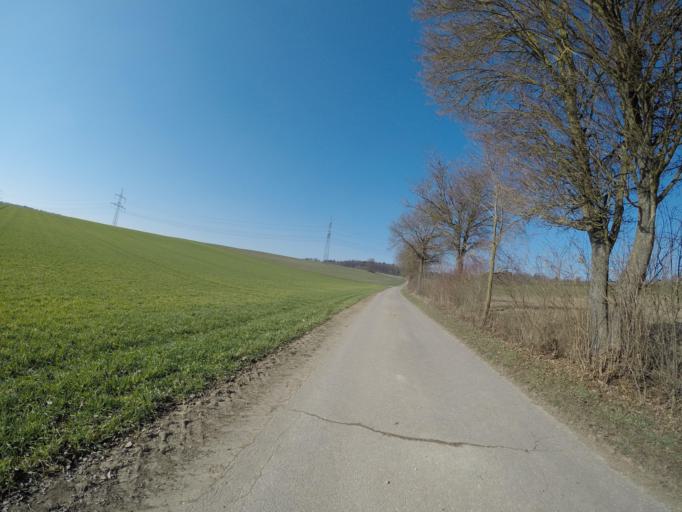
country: DE
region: Baden-Wuerttemberg
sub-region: Tuebingen Region
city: Erbach
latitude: 48.3858
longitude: 9.8505
